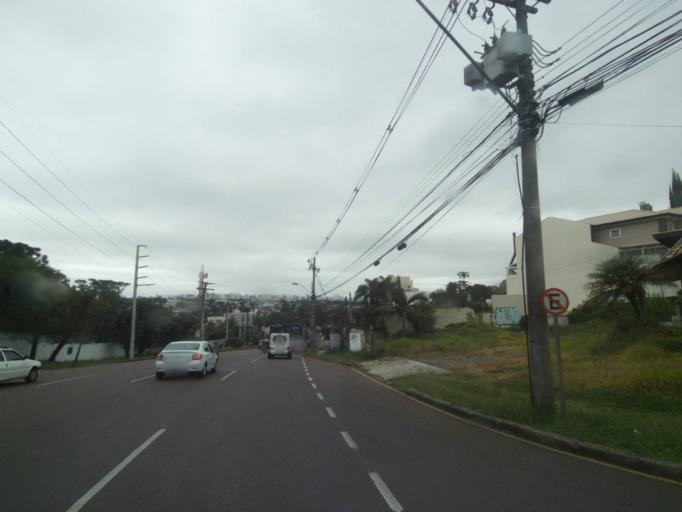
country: BR
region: Parana
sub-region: Curitiba
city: Curitiba
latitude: -25.4390
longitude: -49.3219
